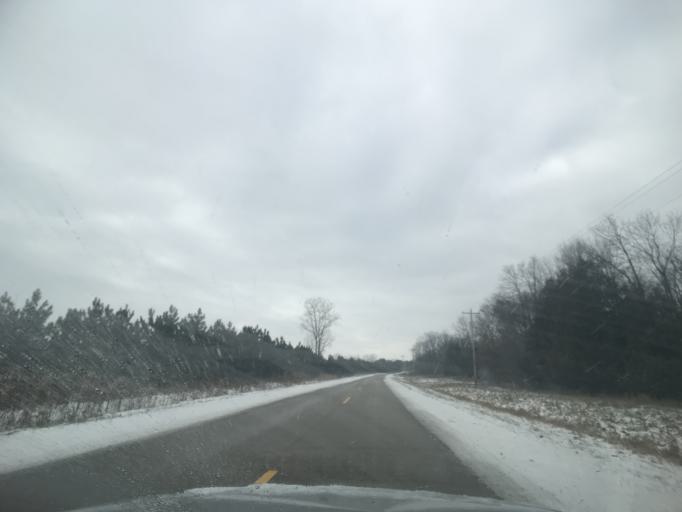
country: US
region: Wisconsin
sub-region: Brown County
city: Suamico
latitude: 44.7060
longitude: -88.0772
